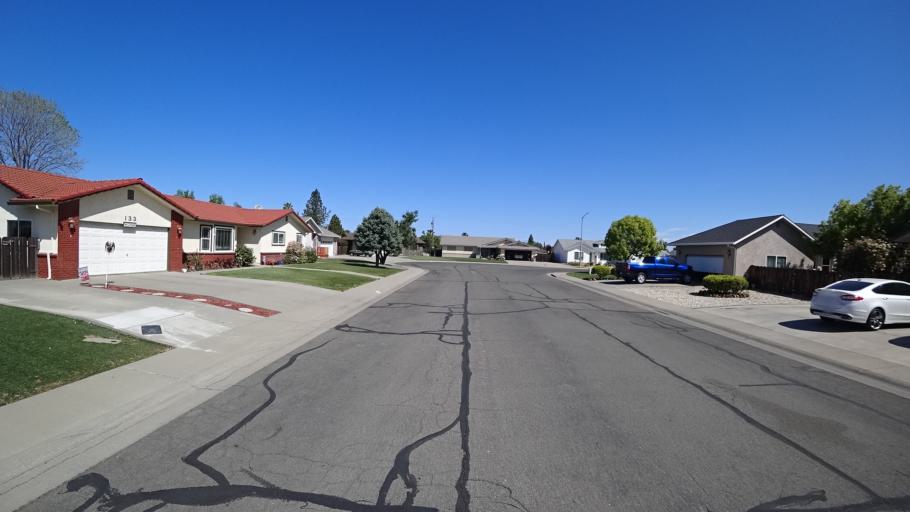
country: US
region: California
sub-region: Glenn County
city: Orland
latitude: 39.7536
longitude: -122.2038
